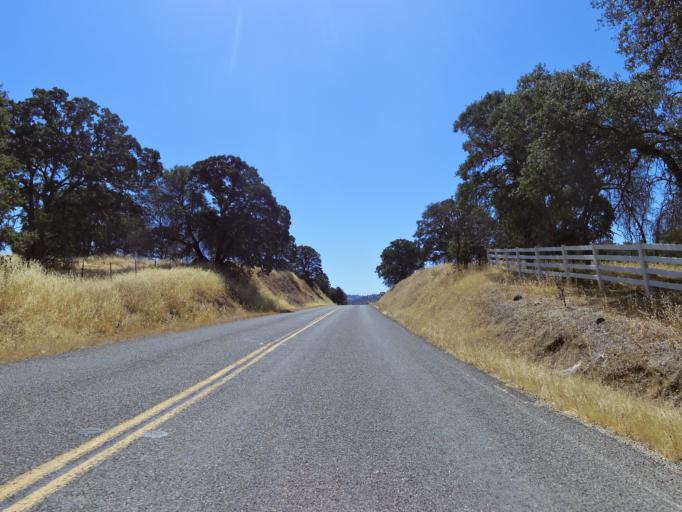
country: US
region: California
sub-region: Mariposa County
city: Mariposa
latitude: 37.4777
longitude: -120.1124
